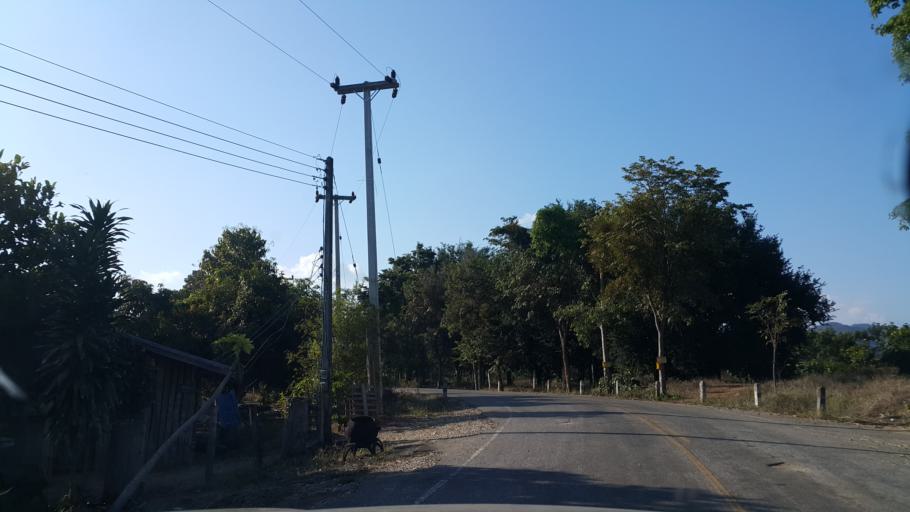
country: TH
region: Sukhothai
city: Thung Saliam
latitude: 17.3878
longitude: 99.5175
